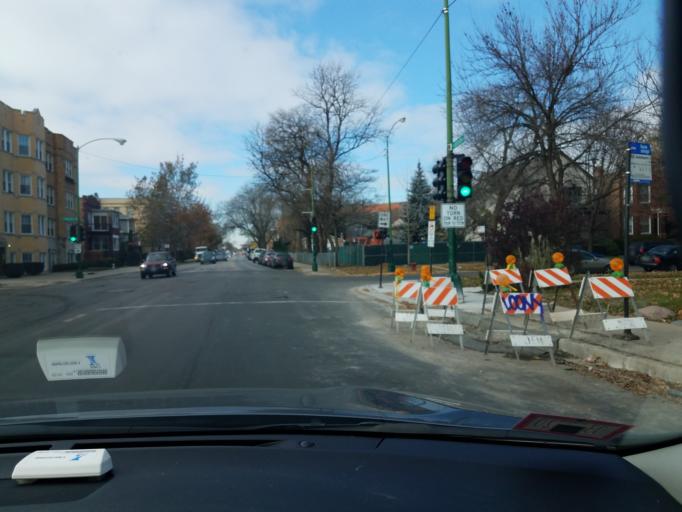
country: US
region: Illinois
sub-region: Cook County
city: Lincolnwood
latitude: 41.9464
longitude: -87.7319
